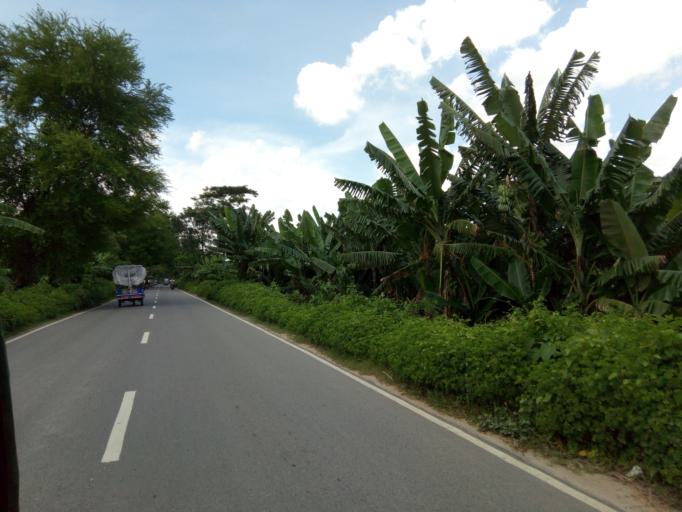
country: BD
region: Dhaka
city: Tungipara
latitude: 22.9595
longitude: 89.8186
